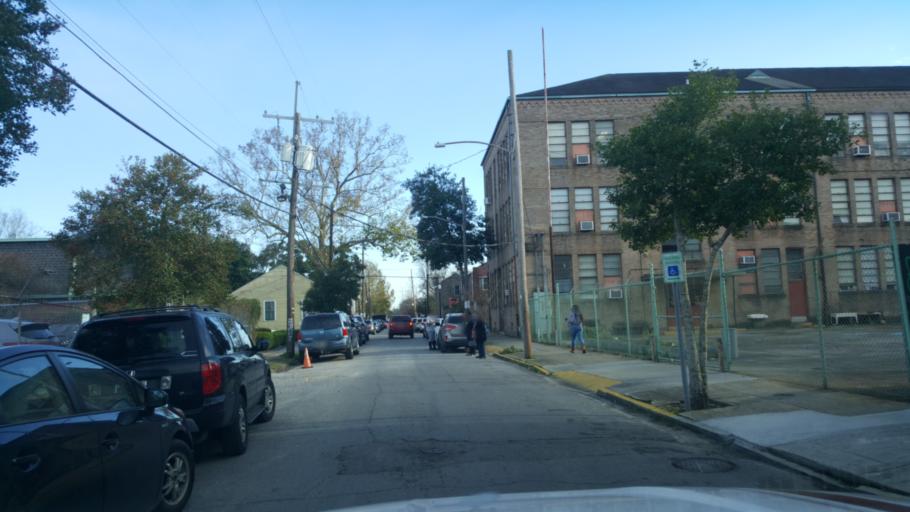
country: US
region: Louisiana
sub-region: Orleans Parish
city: New Orleans
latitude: 29.9307
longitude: -90.0743
